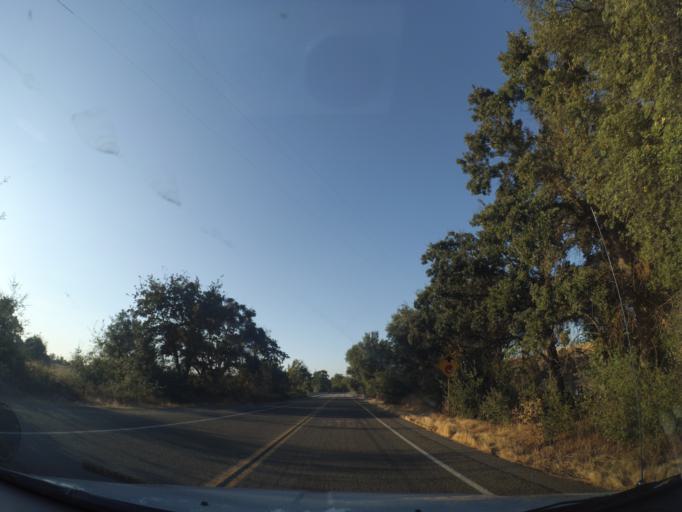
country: US
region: California
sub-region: Merced County
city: Planada
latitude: 37.5234
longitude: -120.3211
